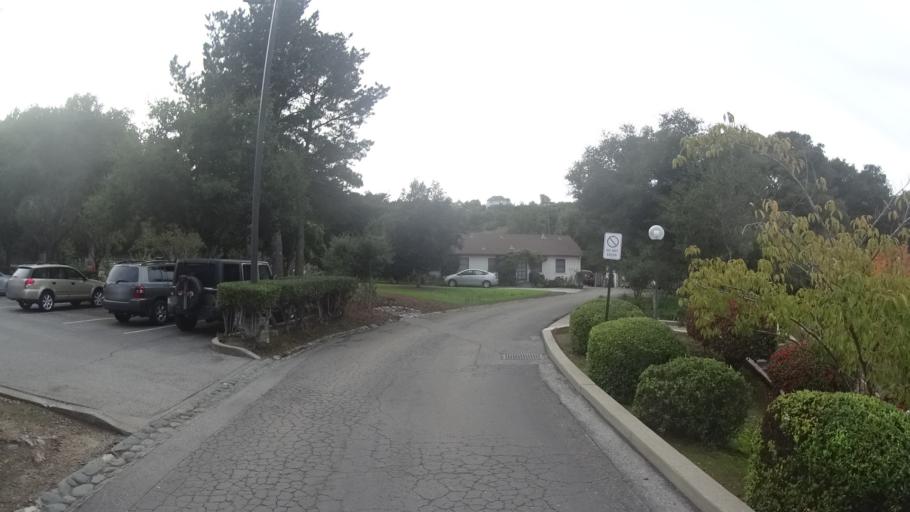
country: US
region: California
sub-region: San Mateo County
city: Hillsborough
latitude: 37.5832
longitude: -122.3849
